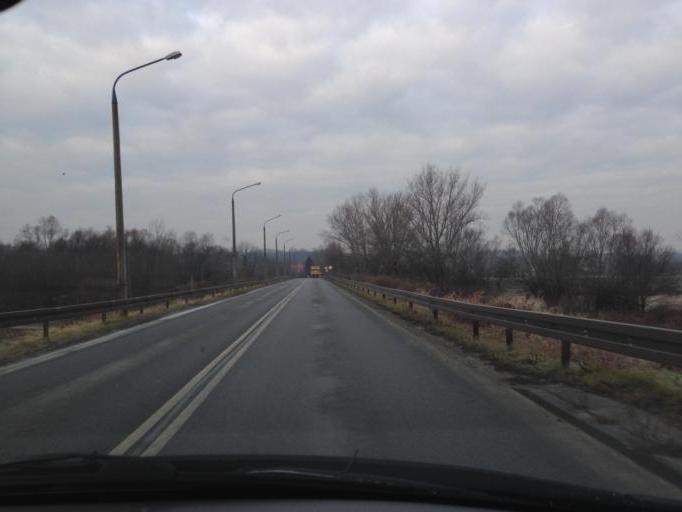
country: PL
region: Lesser Poland Voivodeship
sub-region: Powiat wielicki
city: Kokotow
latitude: 50.0568
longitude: 20.0712
